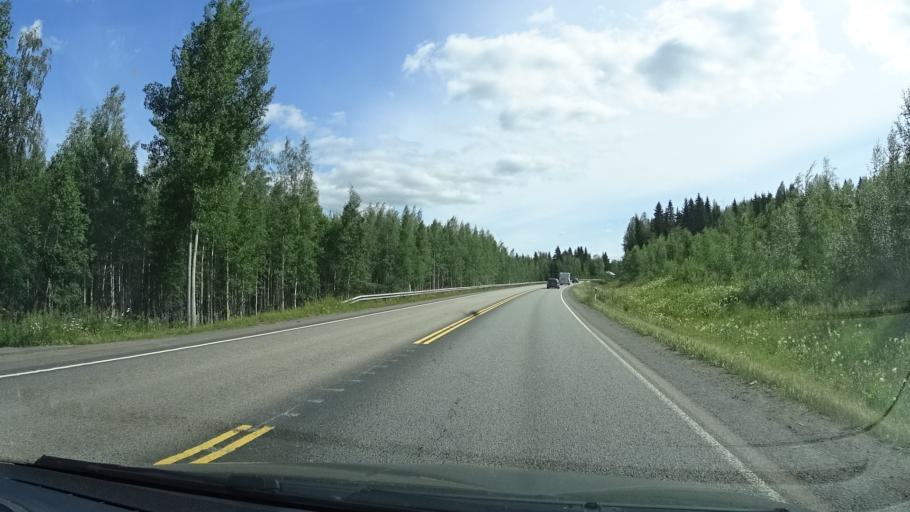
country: FI
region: Central Finland
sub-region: Jyvaeskylae
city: Jyvaeskylae
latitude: 62.2696
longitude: 25.5447
